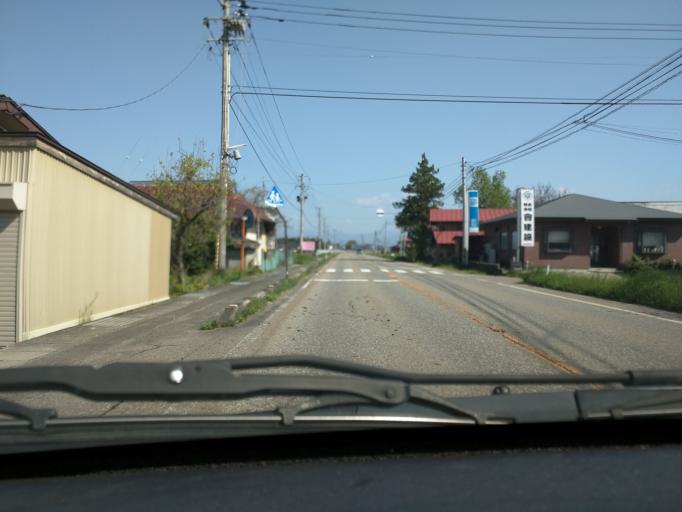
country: JP
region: Fukushima
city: Kitakata
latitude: 37.5564
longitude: 139.9076
